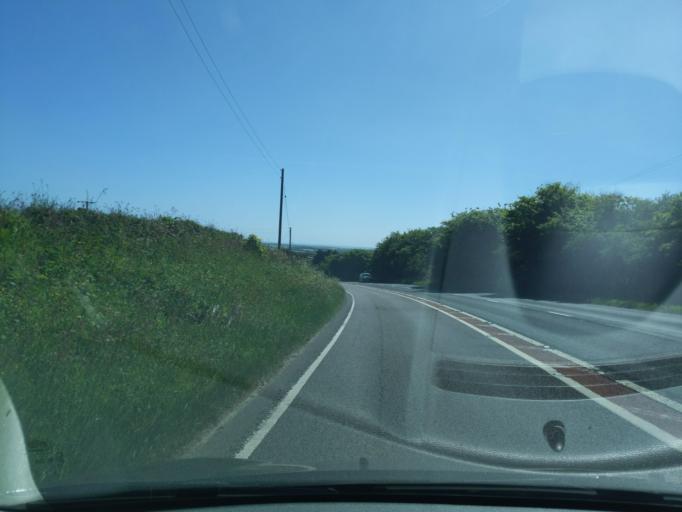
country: GB
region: England
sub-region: Cornwall
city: Wendron
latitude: 50.1295
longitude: -5.2284
